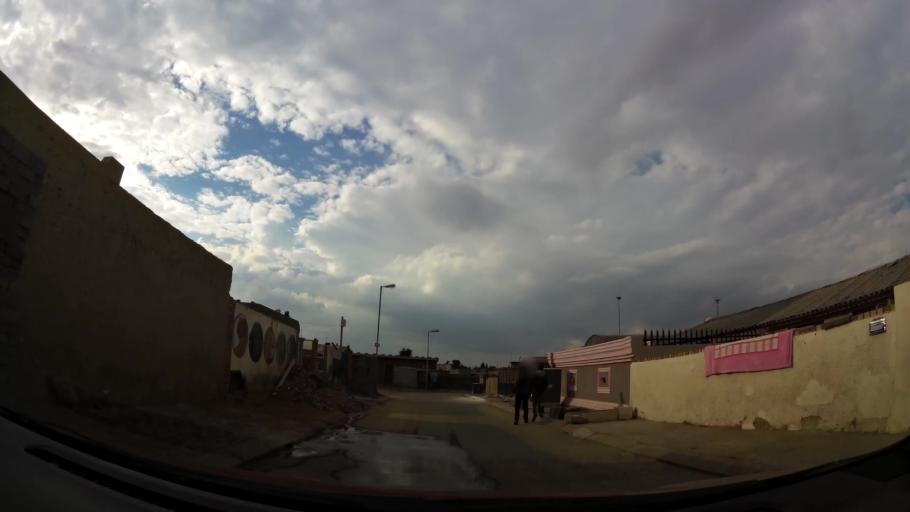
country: ZA
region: Gauteng
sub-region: City of Johannesburg Metropolitan Municipality
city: Soweto
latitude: -26.2530
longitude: 27.8300
